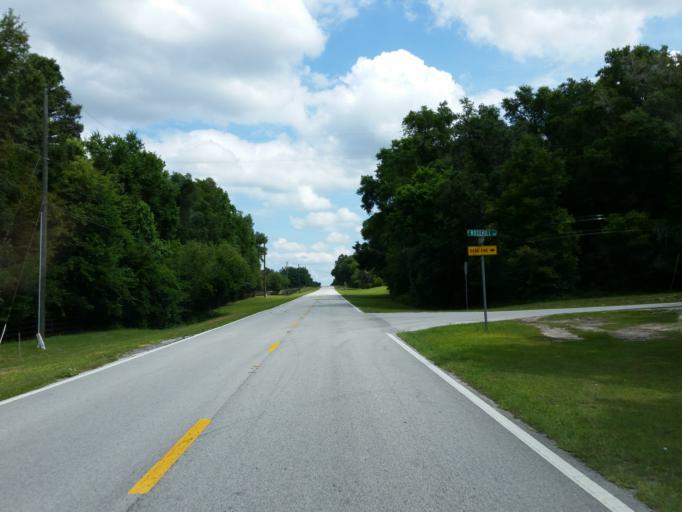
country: US
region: Florida
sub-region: Citrus County
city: Floral City
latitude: 28.6703
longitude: -82.3599
